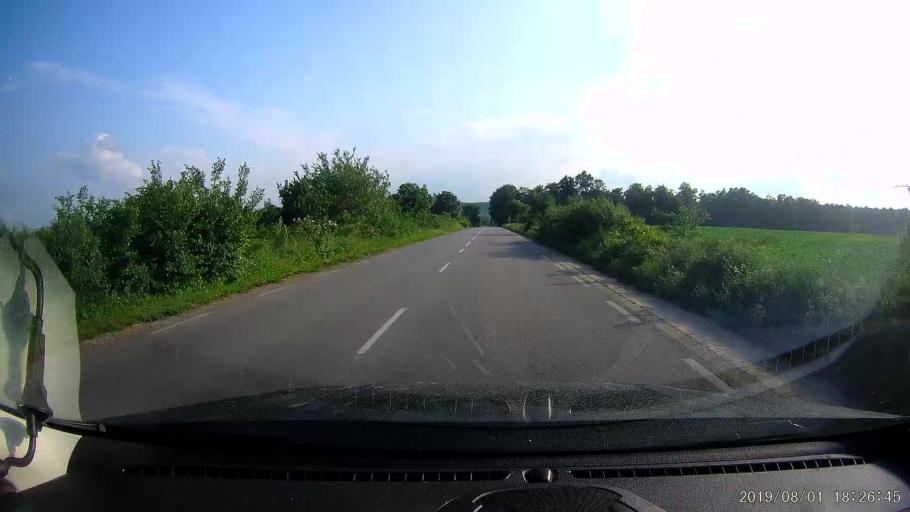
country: BG
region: Shumen
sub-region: Obshtina Venets
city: Venets
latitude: 43.5962
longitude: 26.9866
